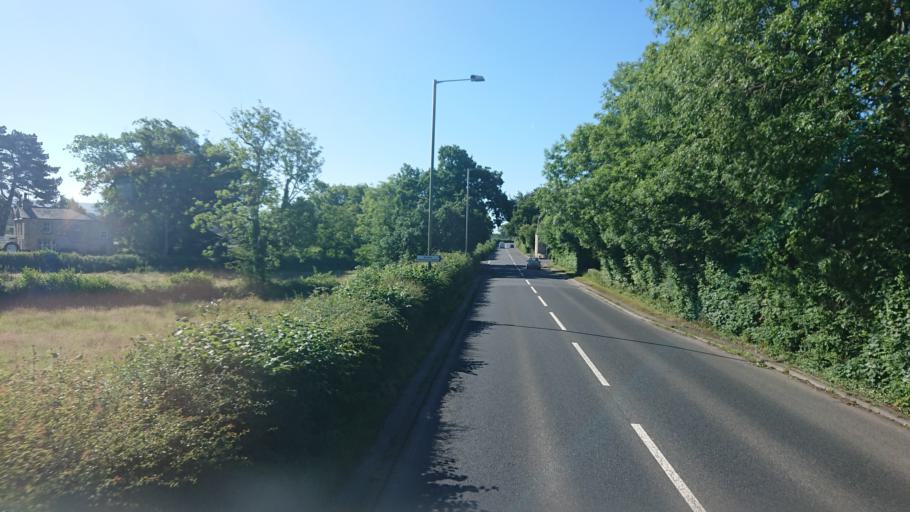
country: GB
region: England
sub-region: Lancashire
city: Bay Horse
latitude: 53.9667
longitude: -2.7792
